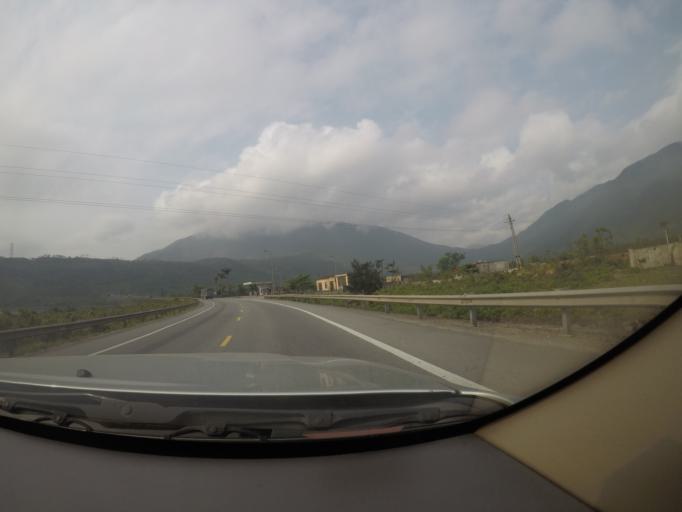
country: VN
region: Ha Tinh
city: Ky Anh
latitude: 17.9652
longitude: 106.4682
